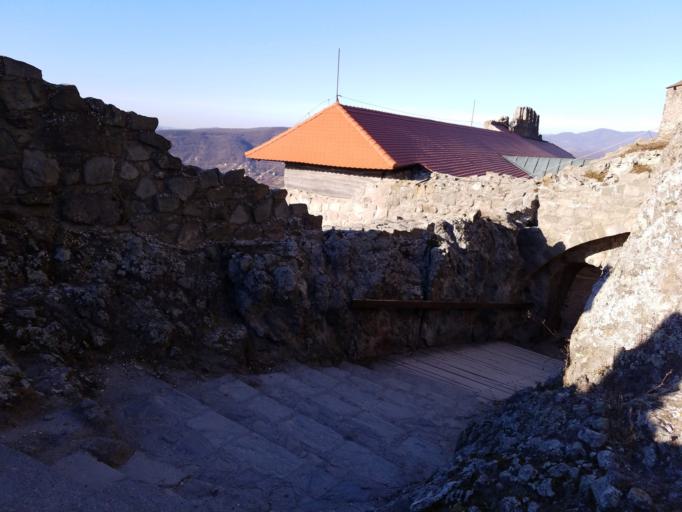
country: HU
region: Pest
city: Visegrad
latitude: 47.7934
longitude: 18.9804
